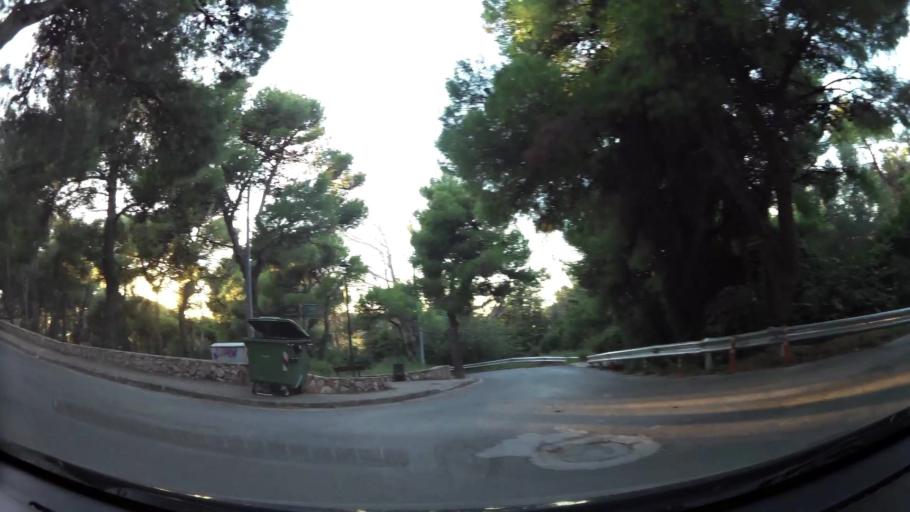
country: GR
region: Attica
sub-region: Nomarchia Athinas
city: Penteli
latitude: 38.0497
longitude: 23.8573
